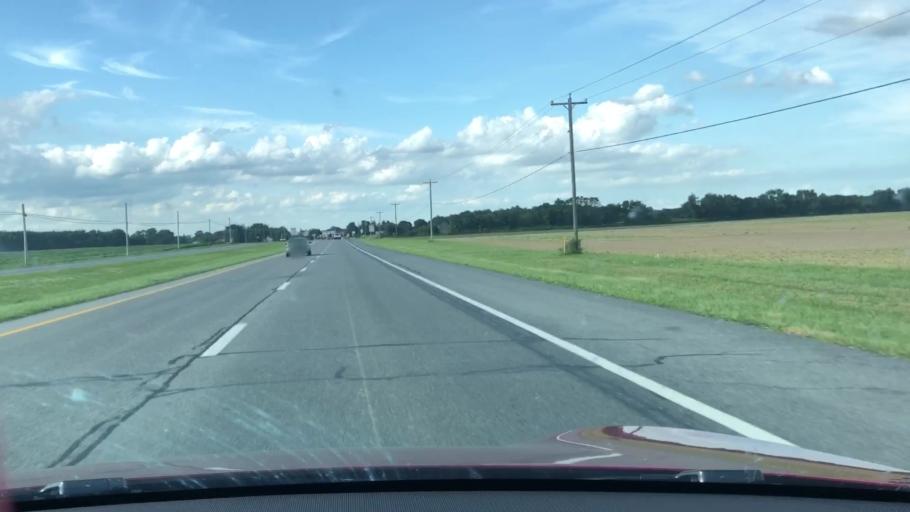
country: US
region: Delaware
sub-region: Kent County
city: Felton
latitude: 38.9975
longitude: -75.5687
